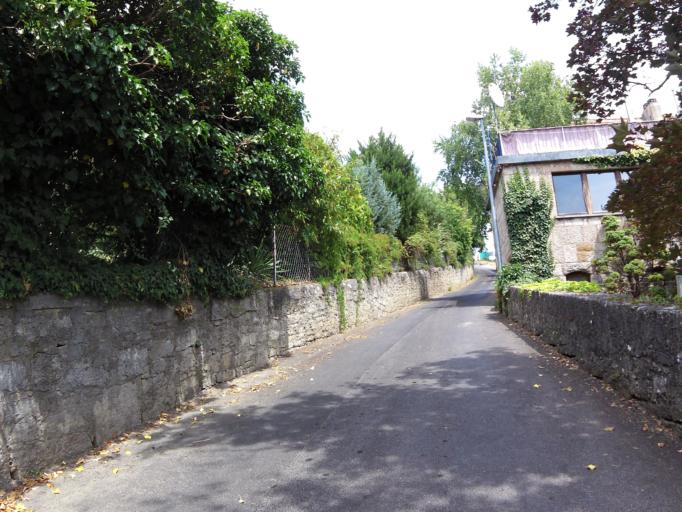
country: DE
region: Bavaria
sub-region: Regierungsbezirk Unterfranken
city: Randersacker
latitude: 49.7614
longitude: 9.9823
